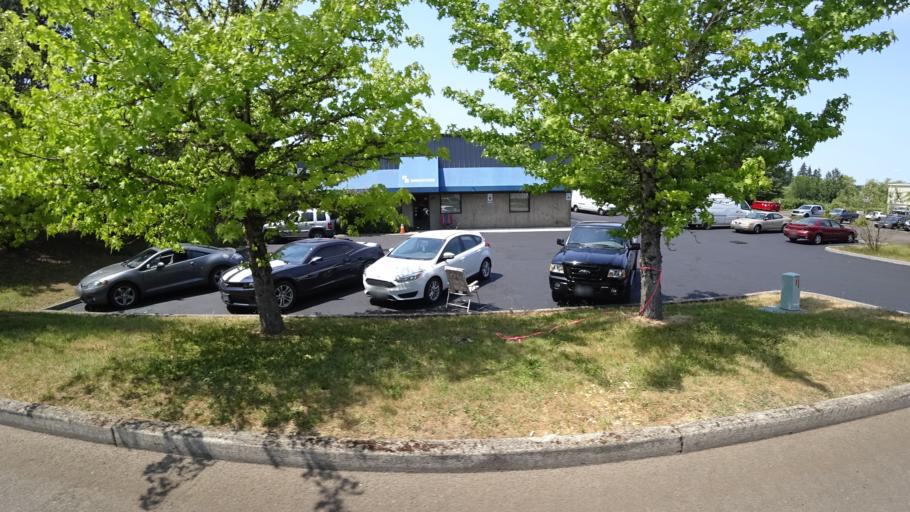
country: US
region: Oregon
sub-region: Washington County
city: Hillsboro
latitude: 45.5002
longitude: -122.9448
